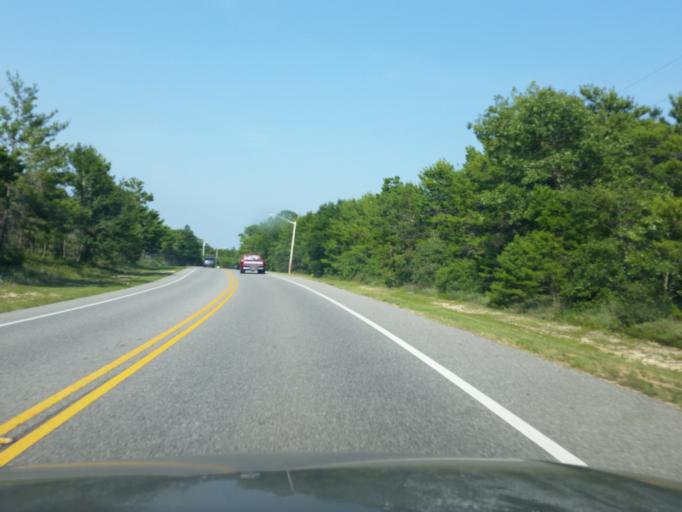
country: US
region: Alabama
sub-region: Baldwin County
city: Gulf Shores
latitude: 30.2526
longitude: -87.7447
